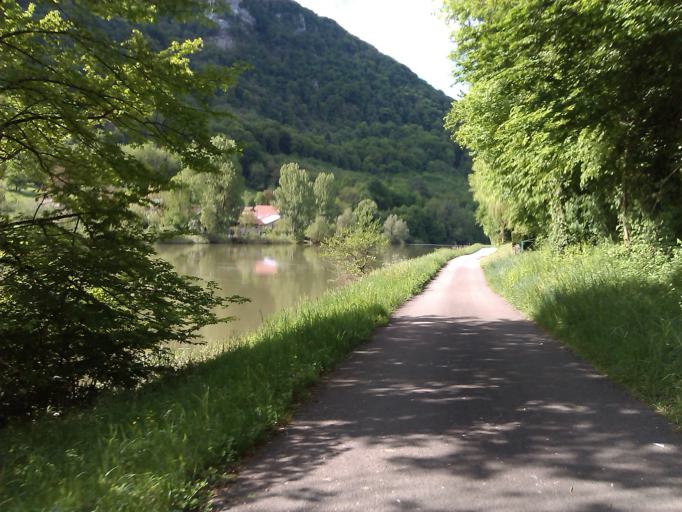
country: FR
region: Franche-Comte
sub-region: Departement du Doubs
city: Roulans
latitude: 47.3236
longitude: 6.2849
